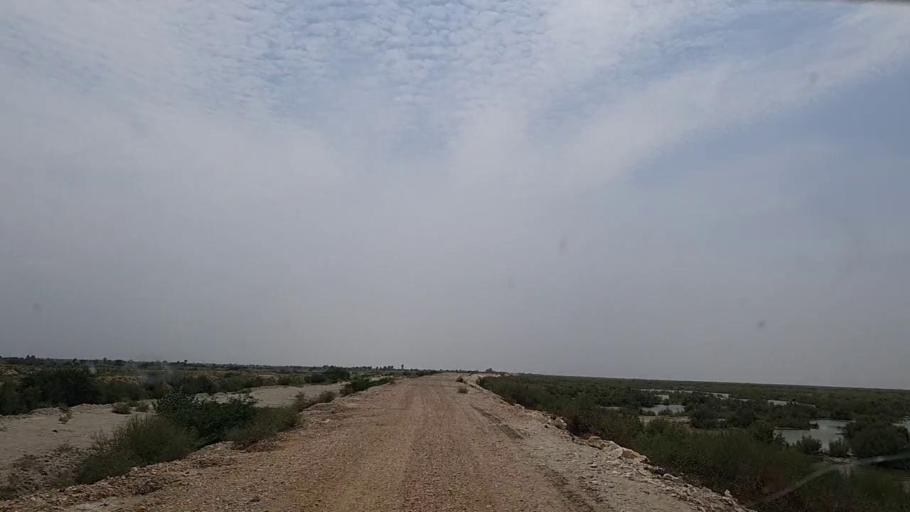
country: PK
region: Sindh
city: Phulji
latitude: 26.8671
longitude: 67.6450
